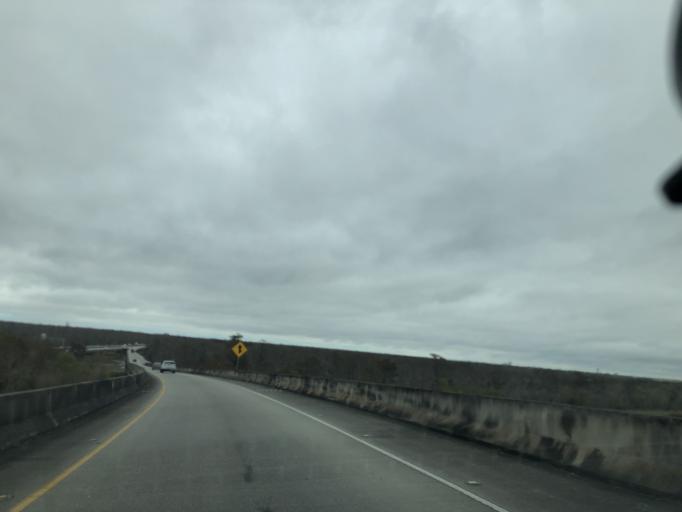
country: US
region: Louisiana
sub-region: Saint Charles Parish
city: Saint Rose
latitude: 29.9755
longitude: -90.3169
